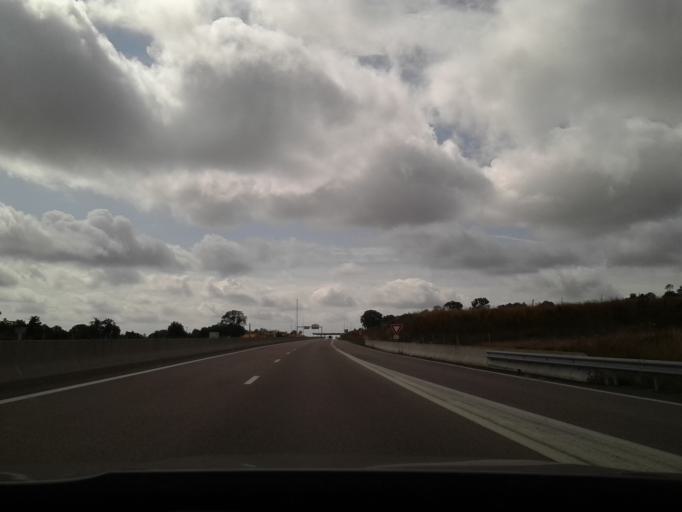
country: FR
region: Lower Normandy
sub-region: Departement de l'Orne
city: Courteilles
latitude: 48.8228
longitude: -0.1347
